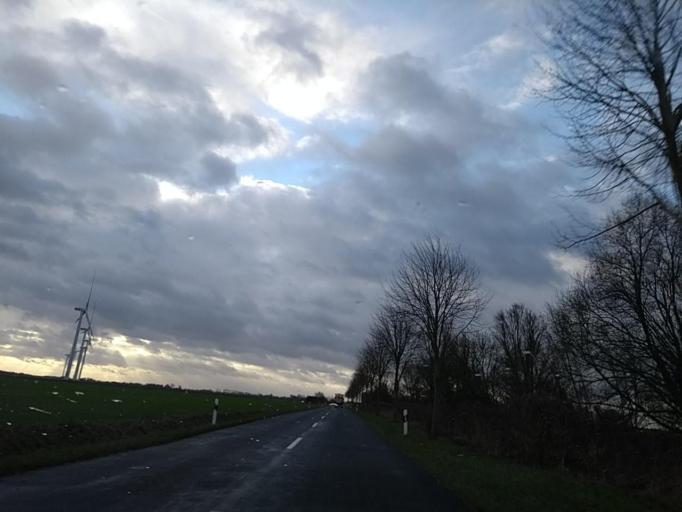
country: DE
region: Lower Saxony
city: Bunde
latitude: 53.2099
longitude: 7.2201
